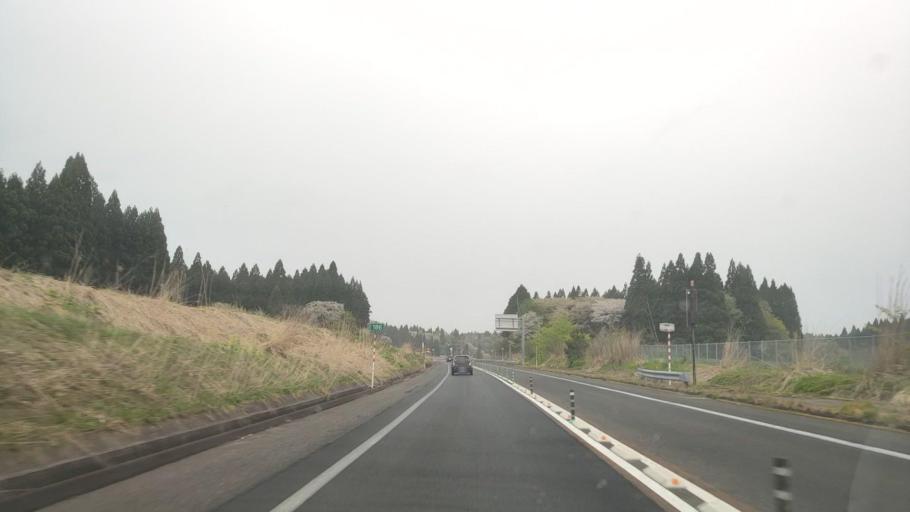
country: JP
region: Akita
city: Noshiromachi
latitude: 40.2084
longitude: 140.1882
